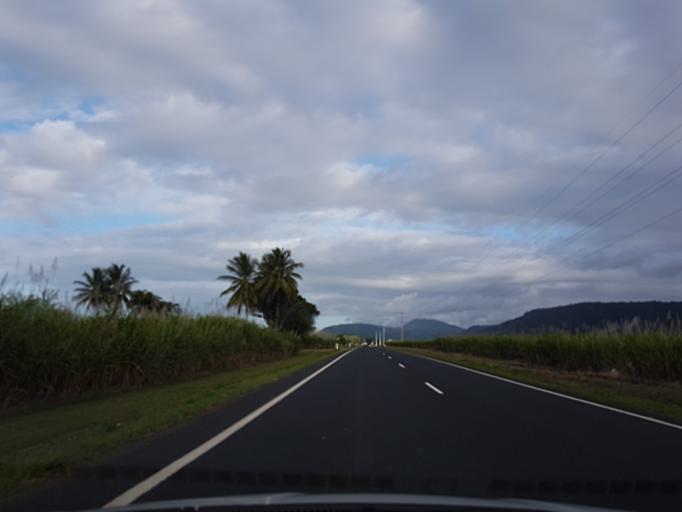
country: AU
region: Queensland
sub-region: Cairns
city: Port Douglas
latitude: -16.5138
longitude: 145.4455
